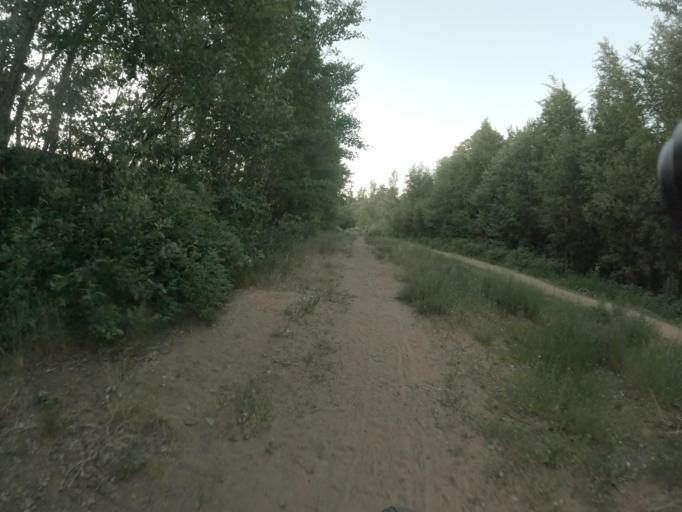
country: RU
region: St.-Petersburg
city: Krasnogvargeisky
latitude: 59.9860
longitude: 30.5290
